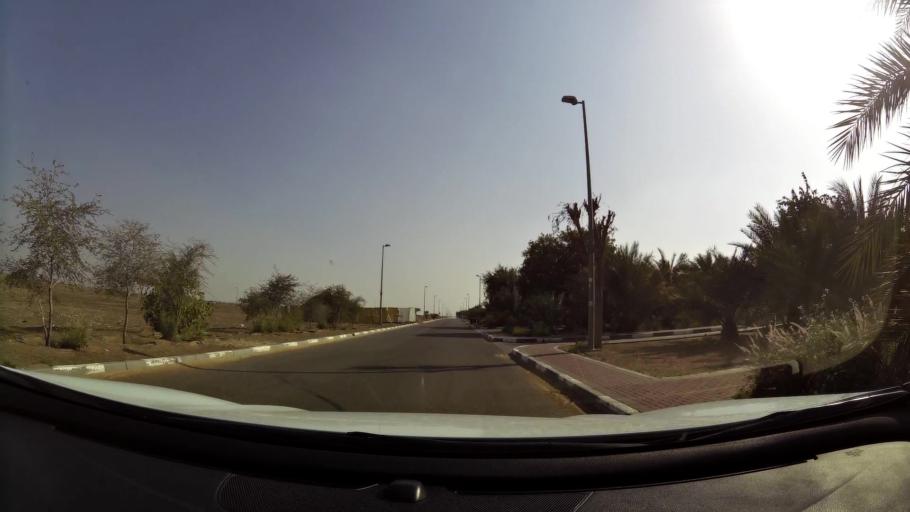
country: AE
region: Abu Dhabi
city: Al Ain
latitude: 24.0796
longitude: 55.8730
